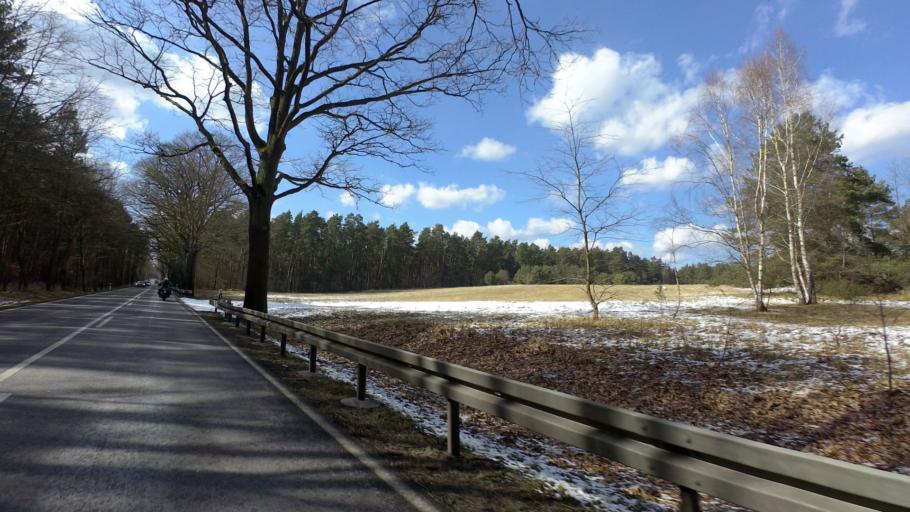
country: DE
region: Brandenburg
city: Marienwerder
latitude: 52.8561
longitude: 13.6388
